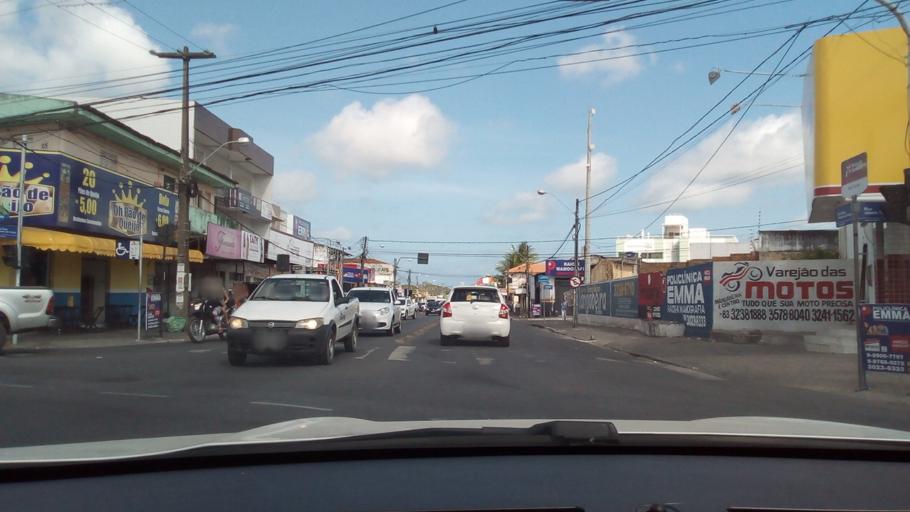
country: BR
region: Paraiba
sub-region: Joao Pessoa
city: Joao Pessoa
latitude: -7.1722
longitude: -34.8398
